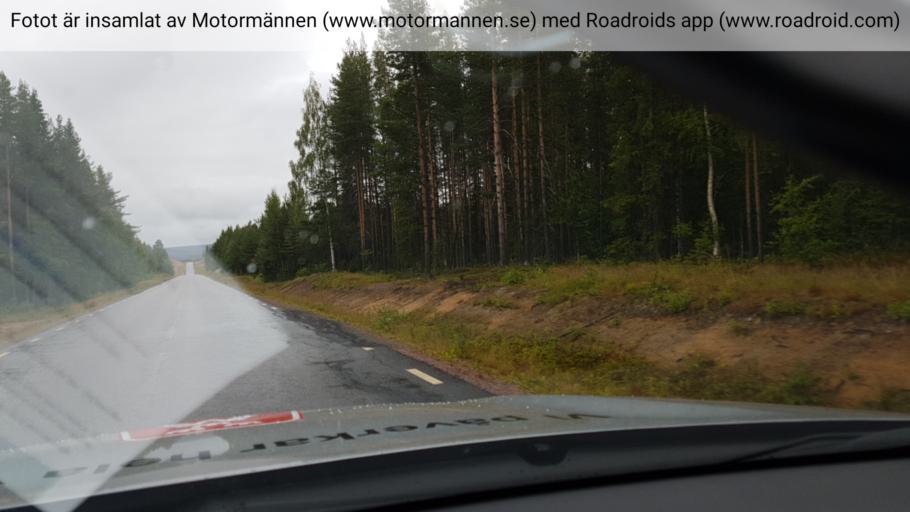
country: SE
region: Norrbotten
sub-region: Gallivare Kommun
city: Gaellivare
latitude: 66.6052
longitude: 20.4585
